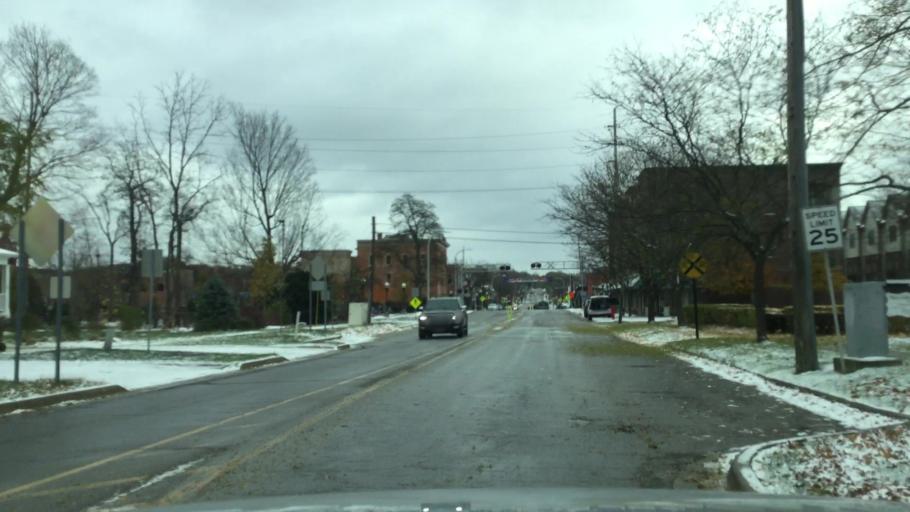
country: US
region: Michigan
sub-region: Livingston County
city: Brighton
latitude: 42.5294
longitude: -83.7871
